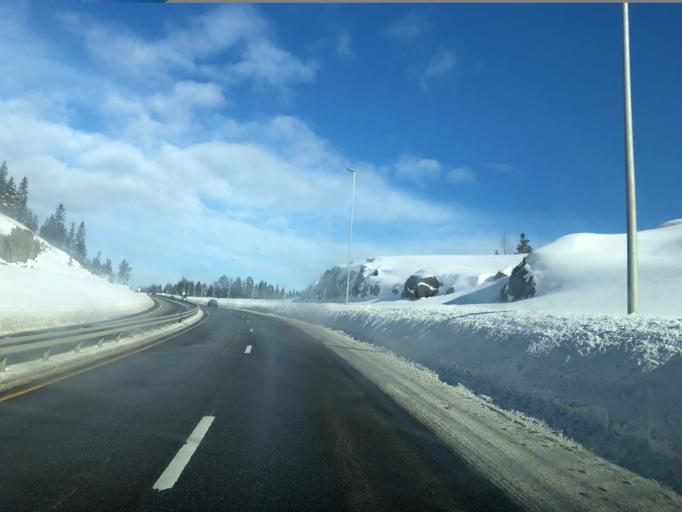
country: NO
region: Oppland
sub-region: Gran
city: Jaren
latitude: 60.4390
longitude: 10.6100
